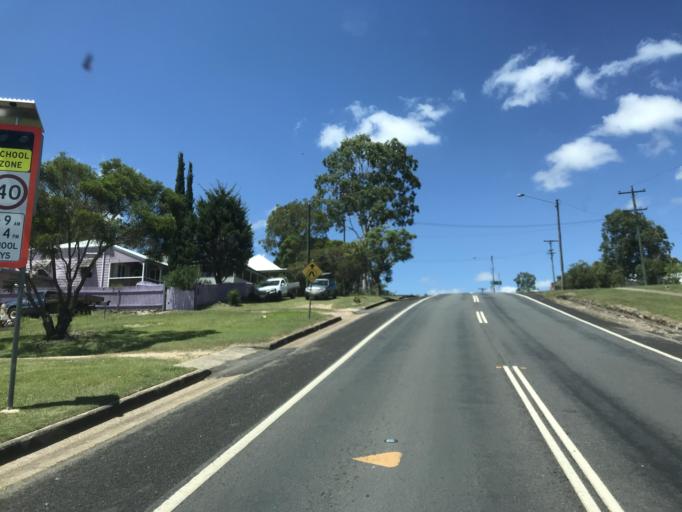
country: AU
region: Queensland
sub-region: Tablelands
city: Atherton
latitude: -17.3808
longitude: 145.3840
